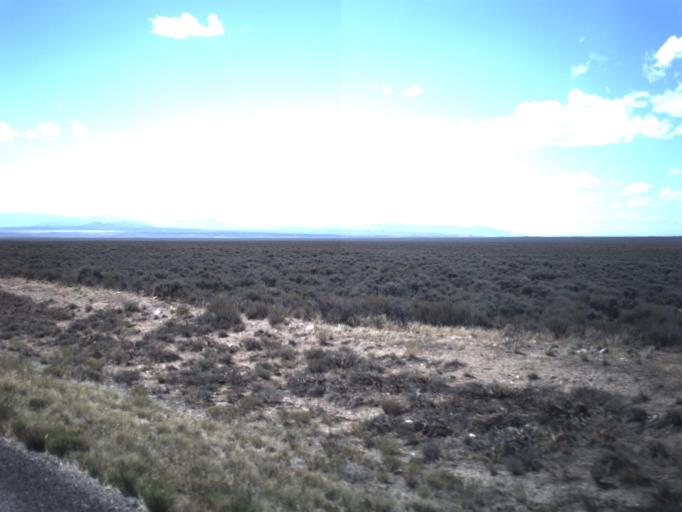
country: US
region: Utah
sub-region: Iron County
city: Enoch
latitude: 37.9799
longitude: -113.0037
